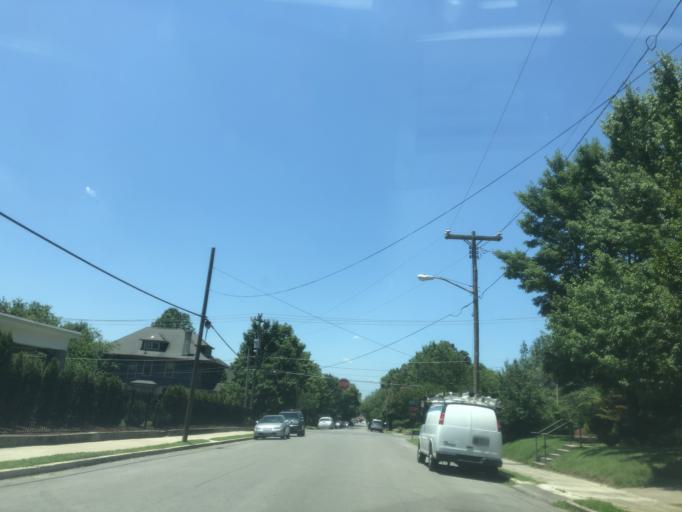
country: US
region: Tennessee
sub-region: Davidson County
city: Nashville
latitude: 36.1822
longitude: -86.7444
